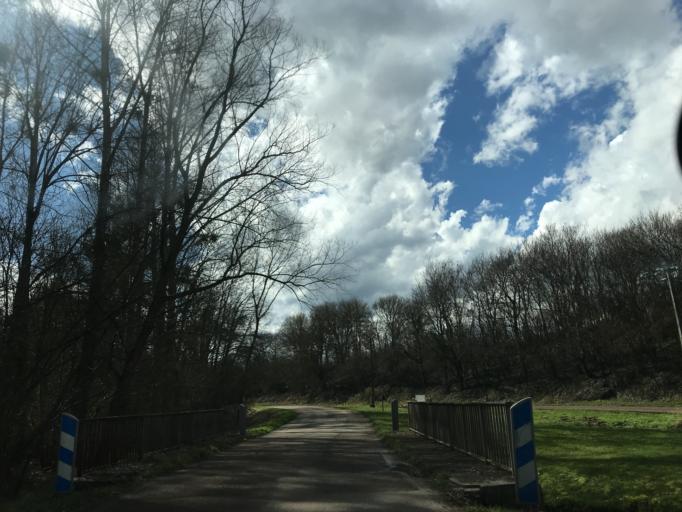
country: FR
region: Bourgogne
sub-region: Departement de la Nievre
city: Clamecy
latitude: 47.5047
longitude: 3.5153
